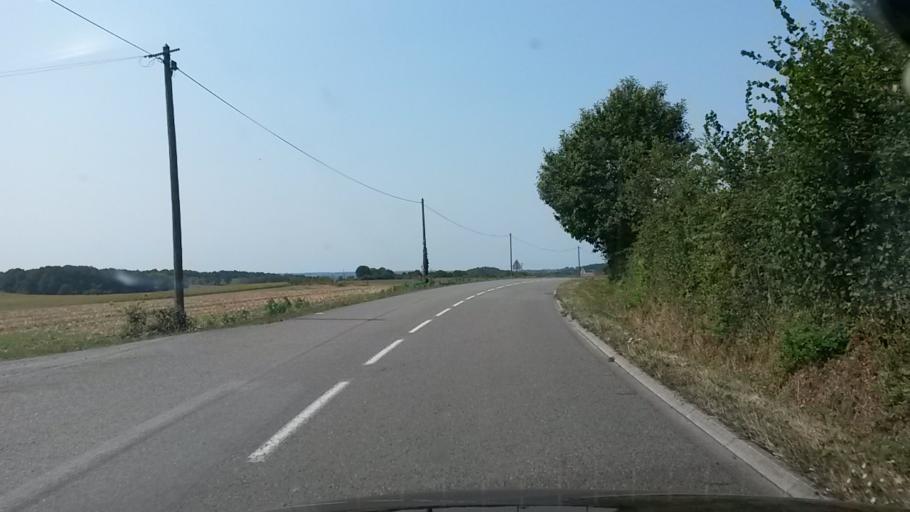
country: FR
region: Pays de la Loire
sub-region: Departement de la Mayenne
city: Courcite
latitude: 48.3588
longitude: -0.2159
